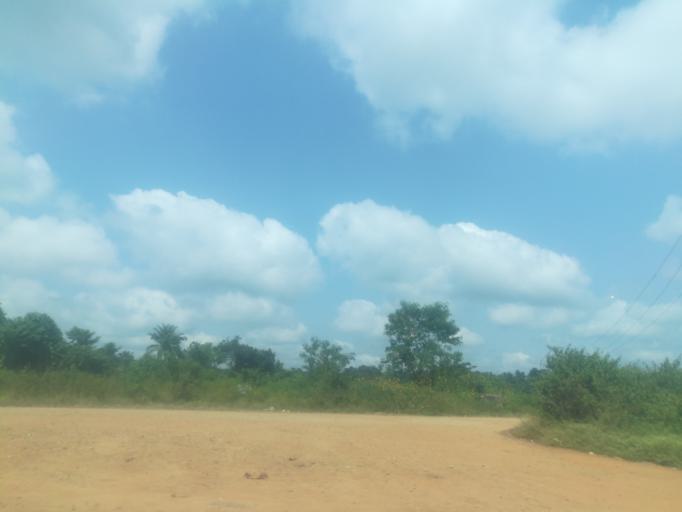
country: NG
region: Oyo
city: Moniya
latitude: 7.5858
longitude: 3.9118
